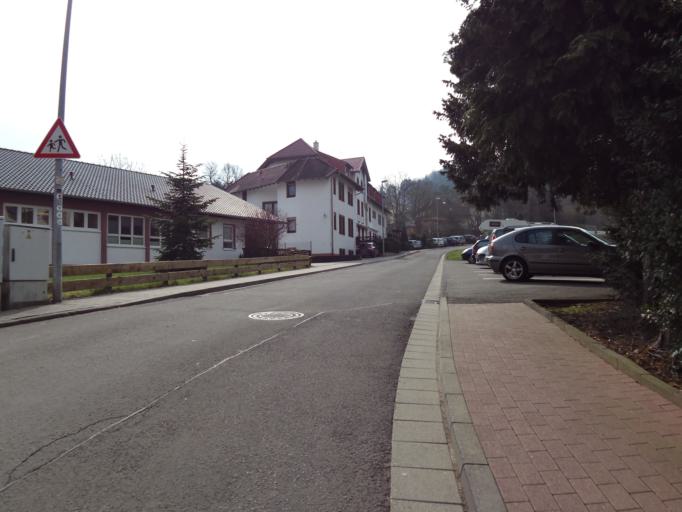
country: DE
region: Rheinland-Pfalz
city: Ramsen
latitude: 49.5353
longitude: 8.0150
